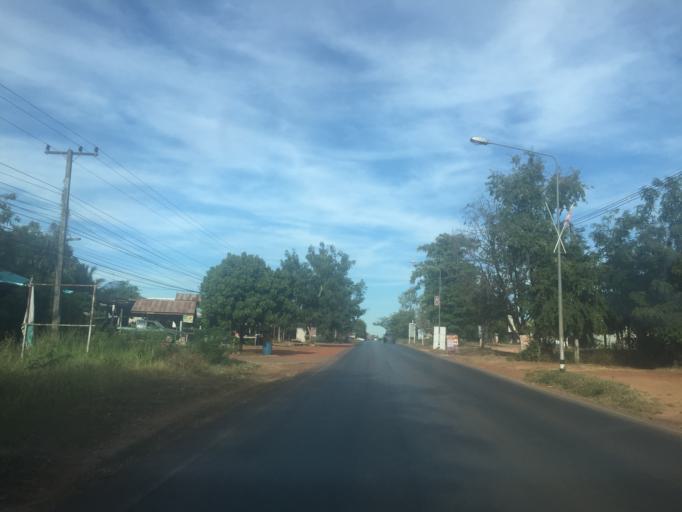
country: TH
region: Changwat Udon Thani
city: Si That
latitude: 16.9815
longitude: 103.1852
